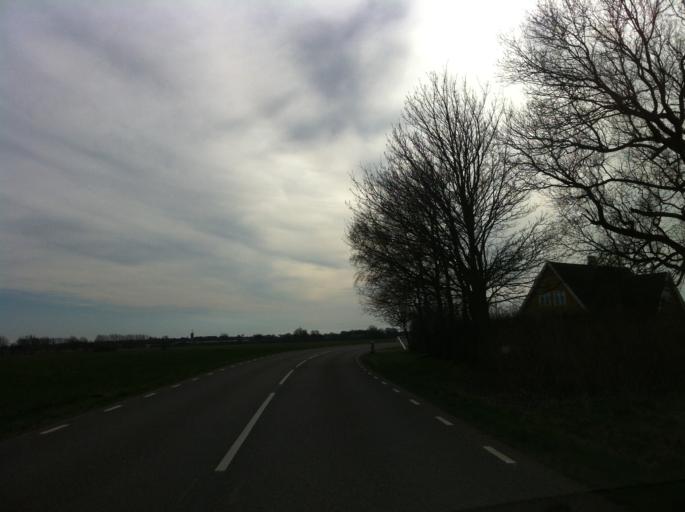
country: SE
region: Skane
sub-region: Hoganas Kommun
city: Hoganas
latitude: 56.2485
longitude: 12.5595
